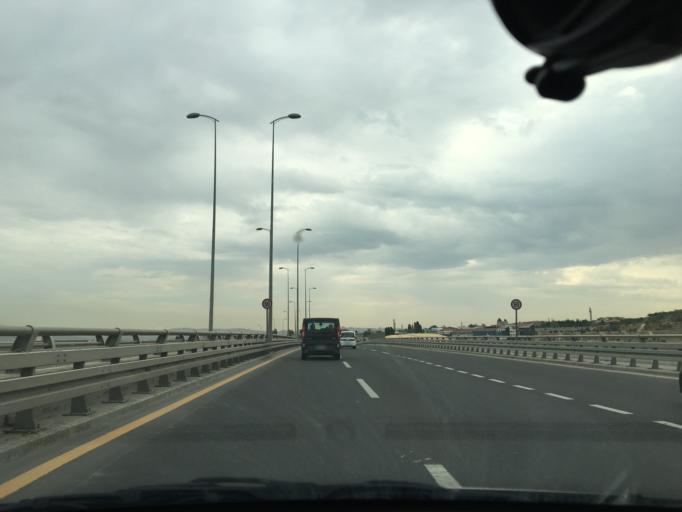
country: TR
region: Ankara
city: Batikent
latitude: 39.9269
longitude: 32.7096
